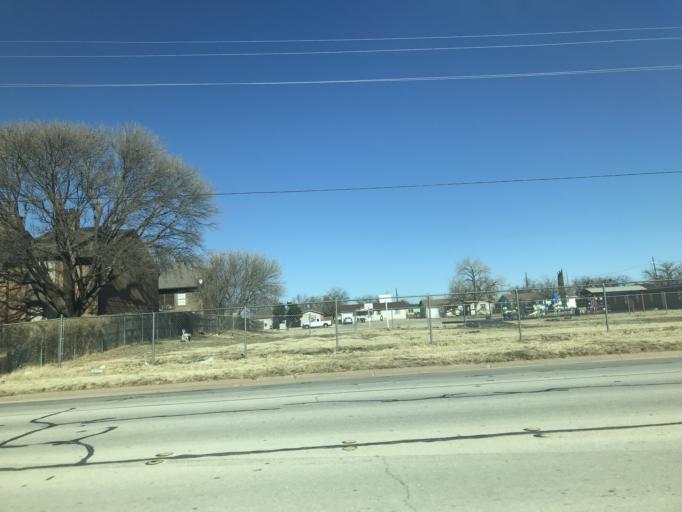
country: US
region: Texas
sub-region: Taylor County
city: Abilene
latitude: 32.4441
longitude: -99.7954
